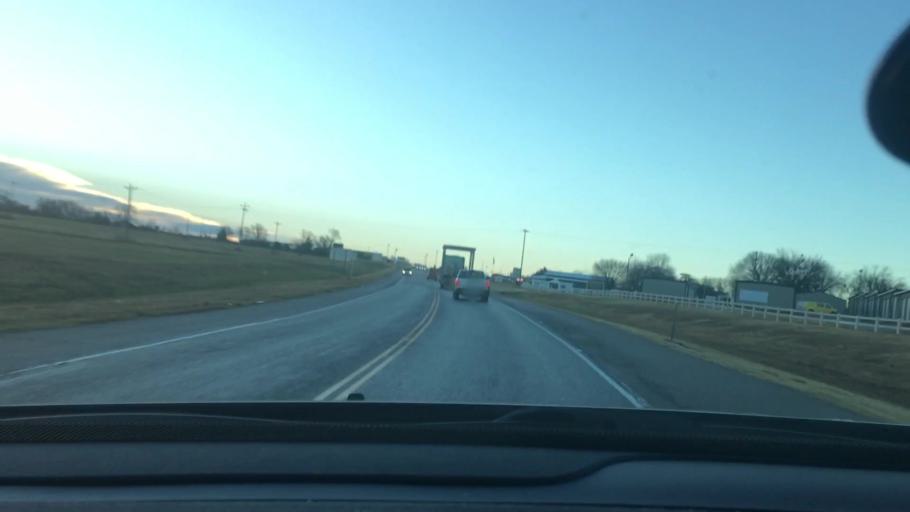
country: US
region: Oklahoma
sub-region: Pontotoc County
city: Ada
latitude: 34.7585
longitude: -96.7034
